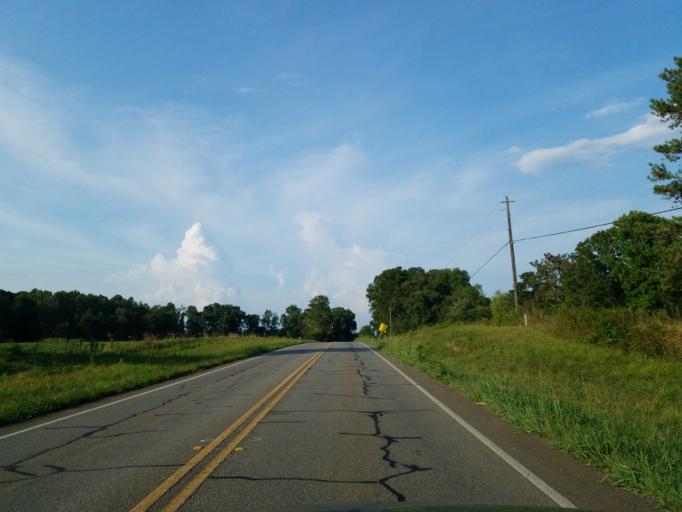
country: US
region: Georgia
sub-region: Pickens County
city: Jasper
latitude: 34.4856
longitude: -84.5797
